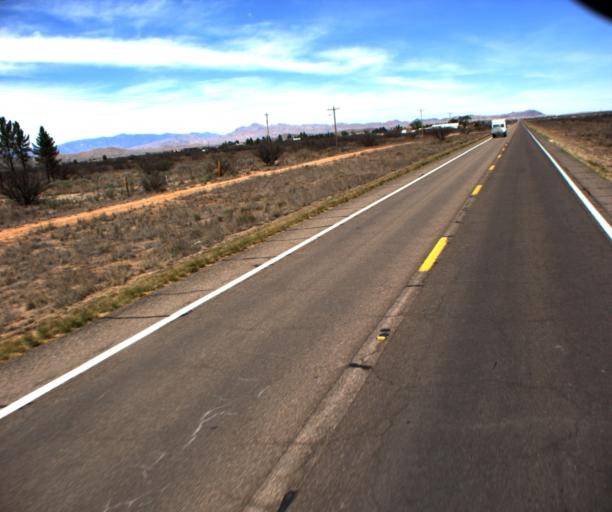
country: US
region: Arizona
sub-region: Cochise County
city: Willcox
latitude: 32.2839
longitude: -109.8107
